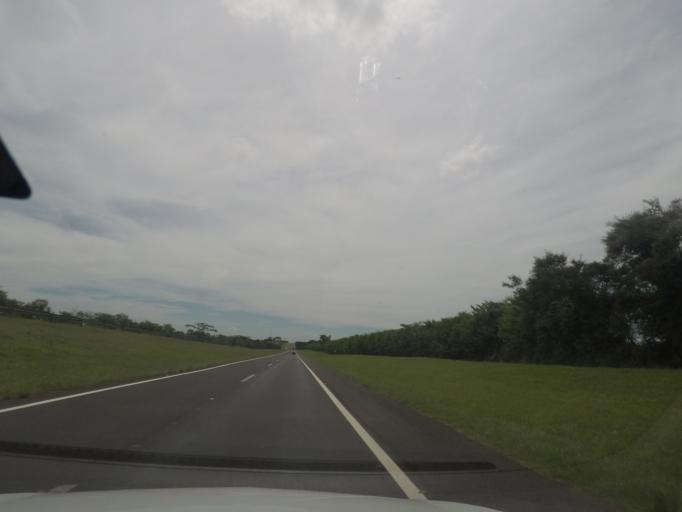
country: BR
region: Sao Paulo
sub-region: Bebedouro
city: Bebedouro
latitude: -20.9796
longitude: -48.4372
